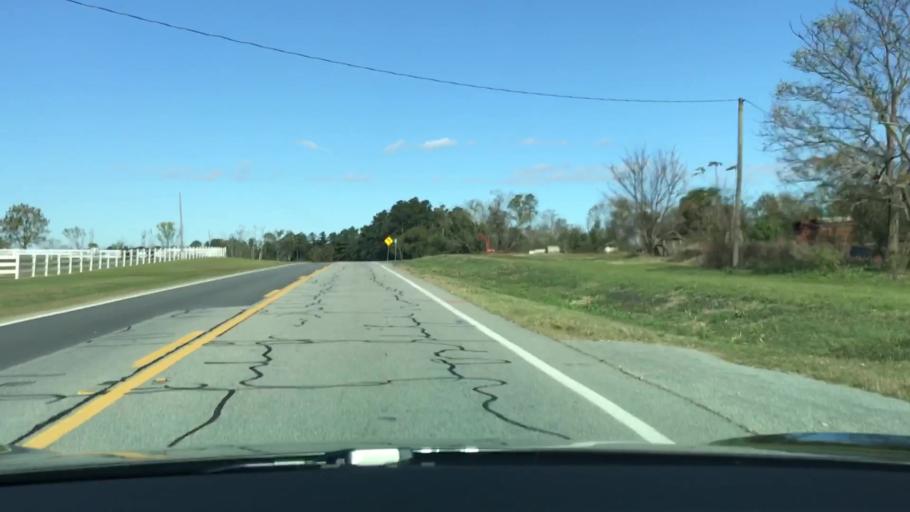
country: US
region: Georgia
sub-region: Warren County
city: Warrenton
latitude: 33.3703
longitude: -82.6011
